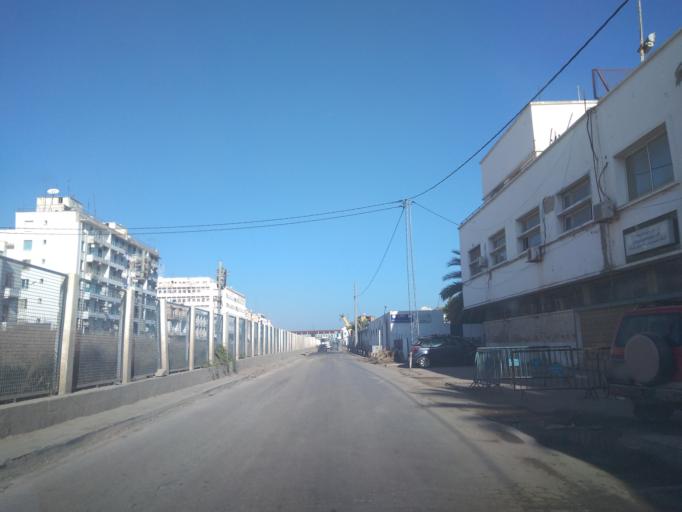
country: TN
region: Safaqis
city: Sfax
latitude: 34.7290
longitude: 10.7651
